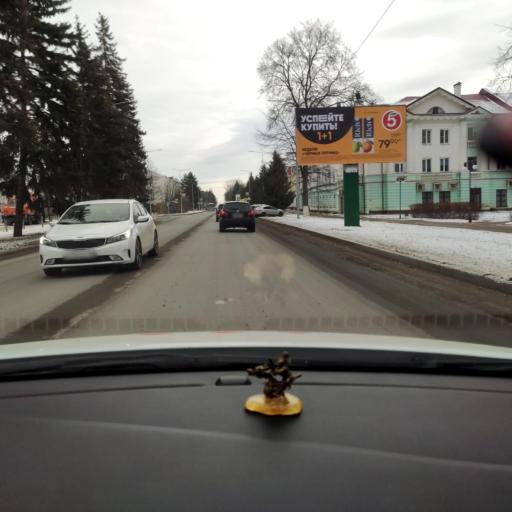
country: RU
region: Tatarstan
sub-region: Zelenodol'skiy Rayon
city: Zelenodolsk
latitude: 55.8459
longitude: 48.5120
